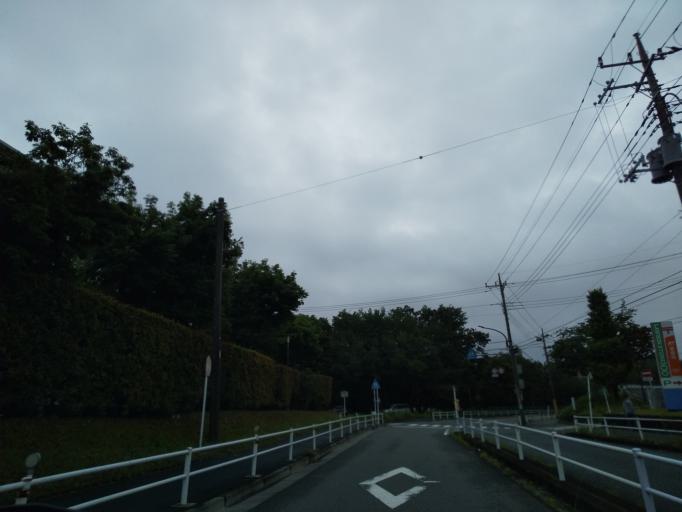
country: JP
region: Tokyo
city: Hino
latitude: 35.6541
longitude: 139.4155
